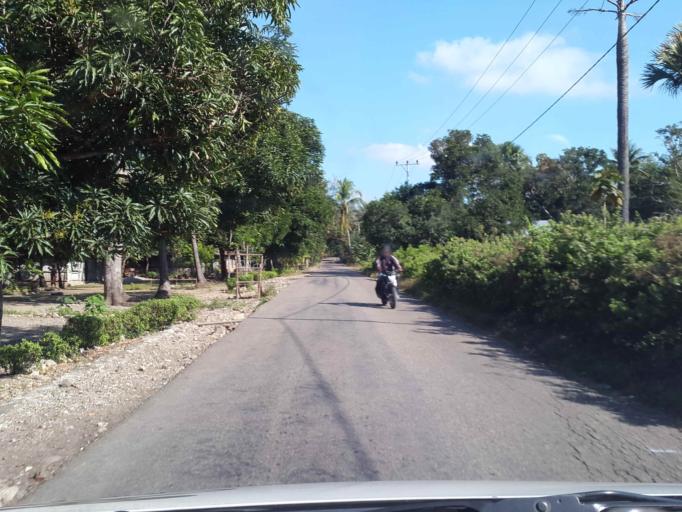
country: ID
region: East Nusa Tenggara
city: Wekmurak
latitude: -9.3780
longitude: 124.8730
